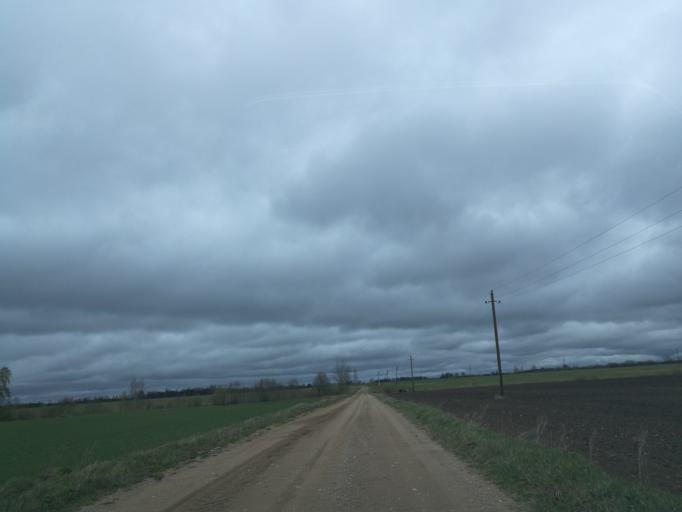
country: LT
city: Ariogala
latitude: 55.3738
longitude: 23.3303
